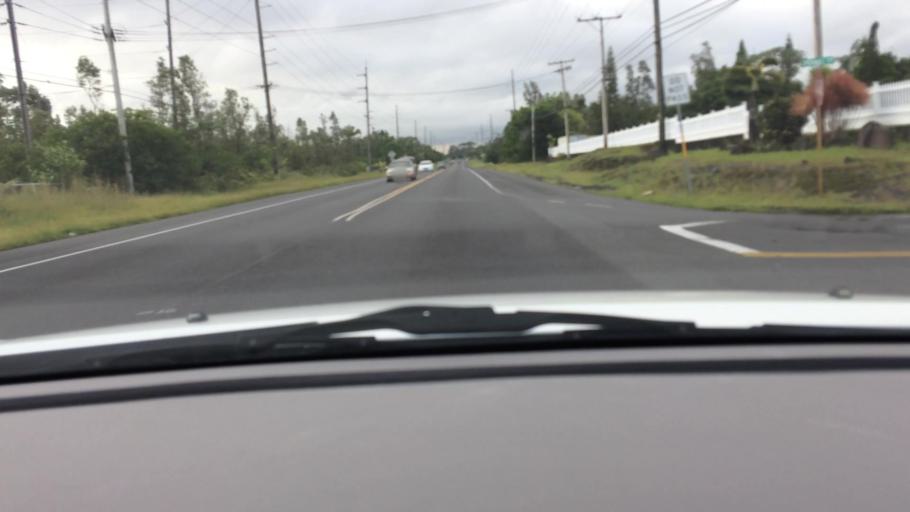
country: US
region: Hawaii
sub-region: Hawaii County
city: Orchidlands Estates
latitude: 19.5666
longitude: -154.9970
